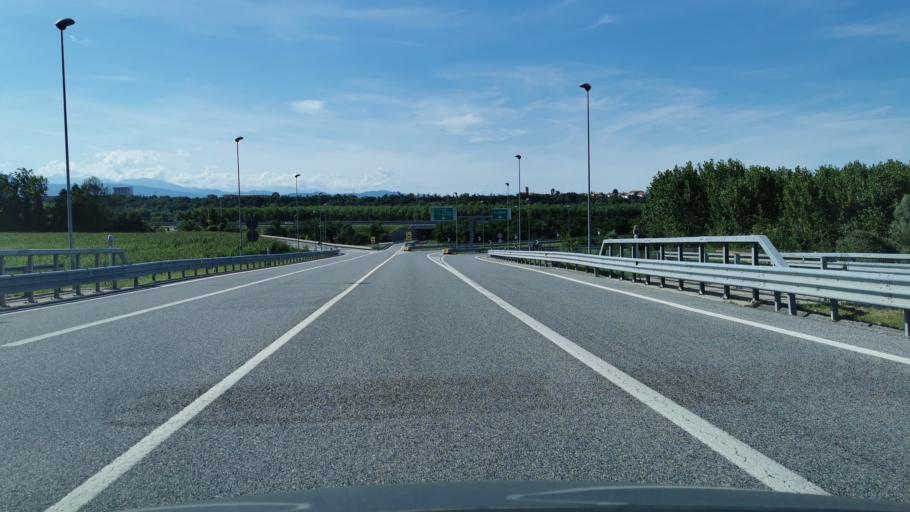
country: IT
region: Piedmont
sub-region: Provincia di Cuneo
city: Castelletto Stura
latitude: 44.4212
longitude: 7.5916
